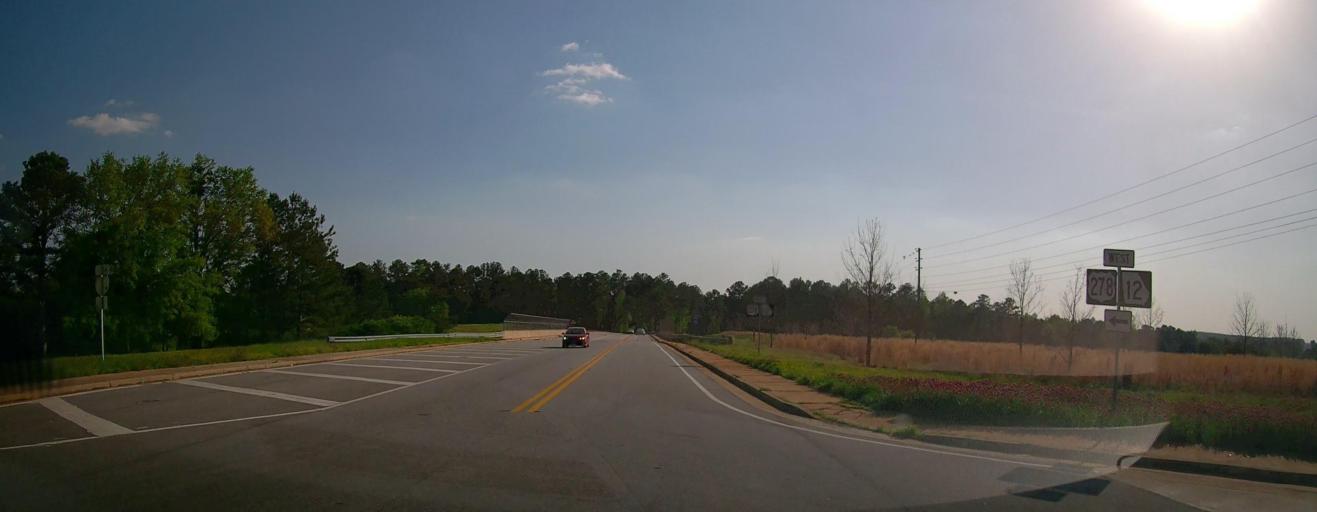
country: US
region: Georgia
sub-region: Walton County
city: Social Circle
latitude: 33.6107
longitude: -83.6984
